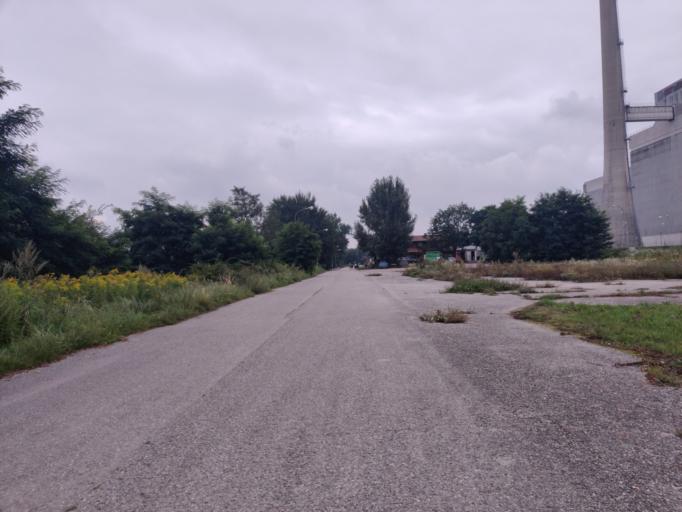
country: AT
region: Lower Austria
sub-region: Politischer Bezirk Tulln
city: Atzenbrugg
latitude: 48.3566
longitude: 15.8843
